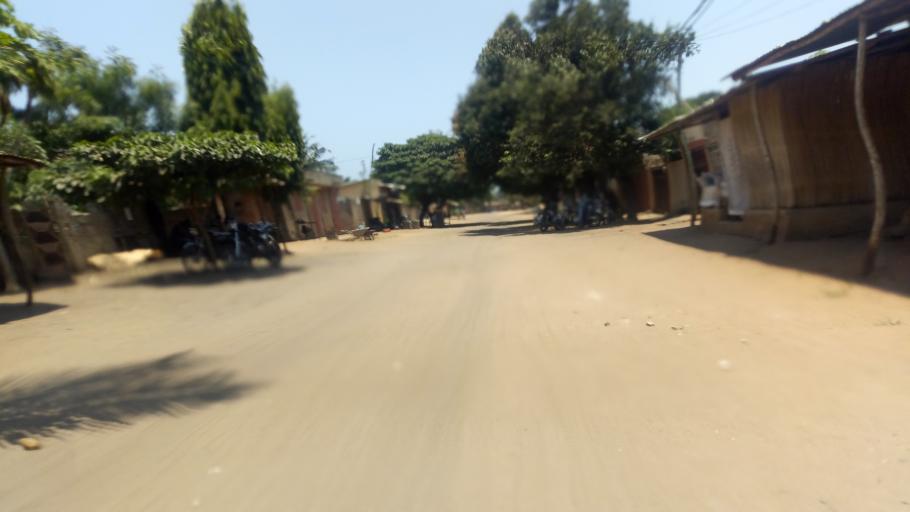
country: TG
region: Maritime
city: Lome
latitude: 6.1891
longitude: 1.1794
